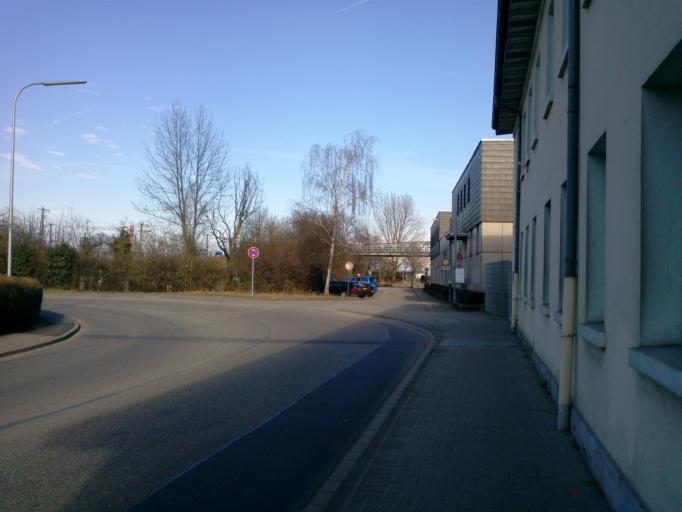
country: DE
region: Baden-Wuerttemberg
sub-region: Karlsruhe Region
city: Karlsruhe
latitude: 48.9945
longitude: 8.4121
